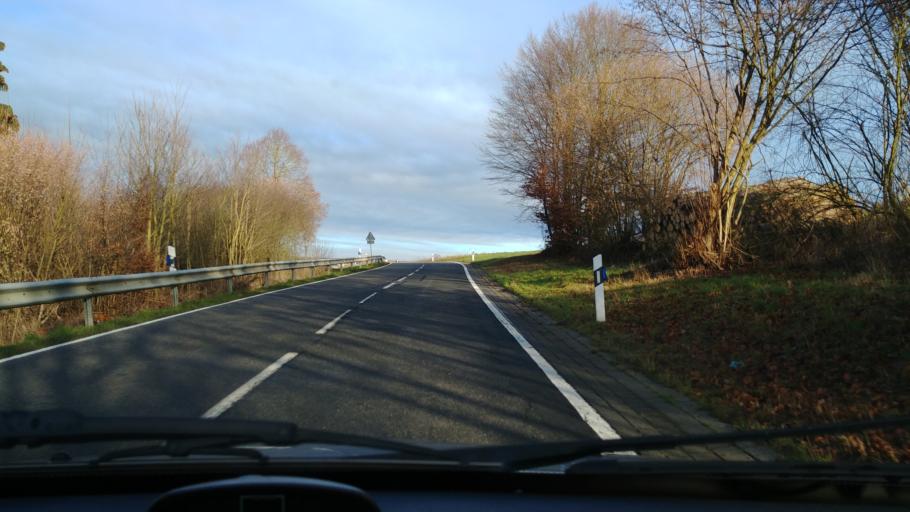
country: DE
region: Rheinland-Pfalz
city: Attenhausen
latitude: 50.2855
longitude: 7.8668
